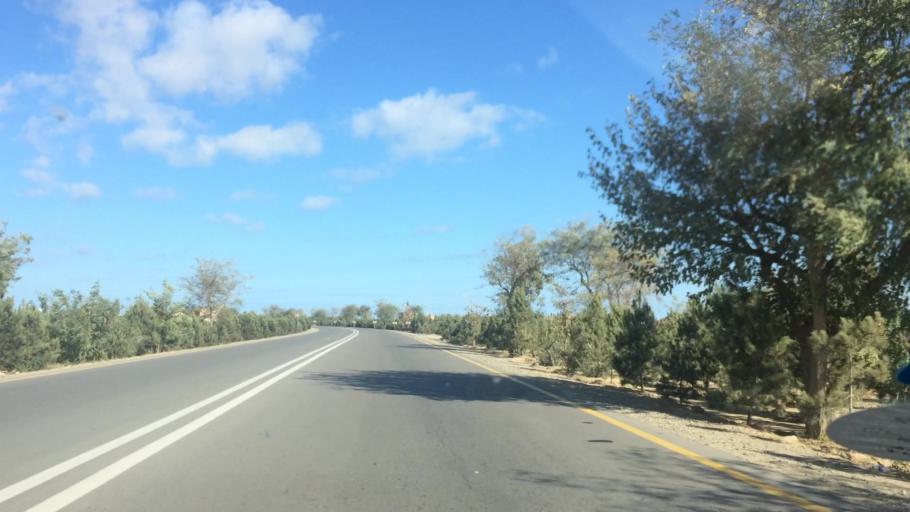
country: AZ
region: Baki
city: Pirallahi
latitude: 40.4212
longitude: 50.3562
